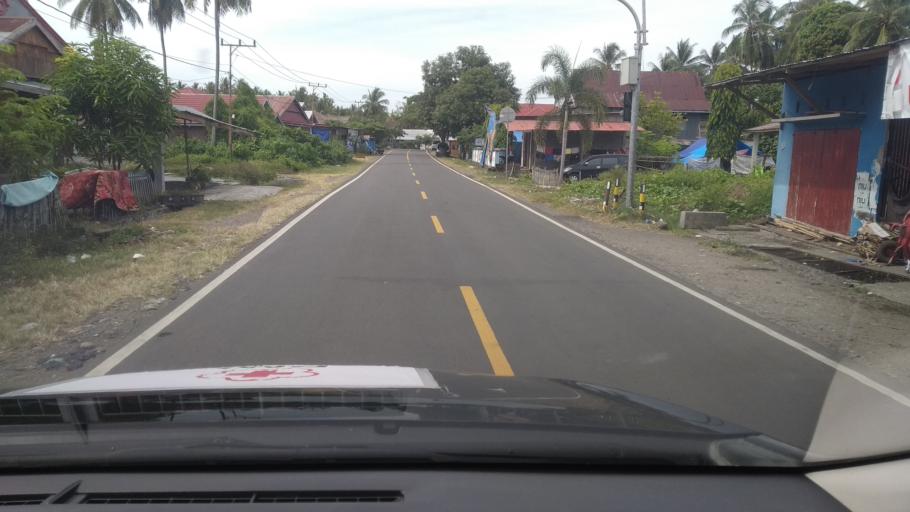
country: ID
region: Sulawesi Barat
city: Malunda
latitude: -3.0092
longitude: 118.8568
